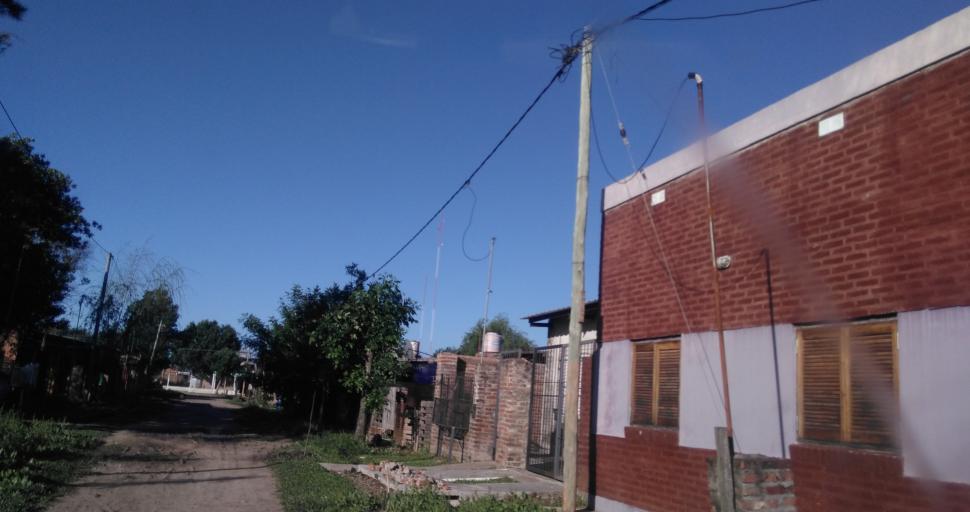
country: AR
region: Chaco
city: Resistencia
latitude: -27.4844
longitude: -59.0015
